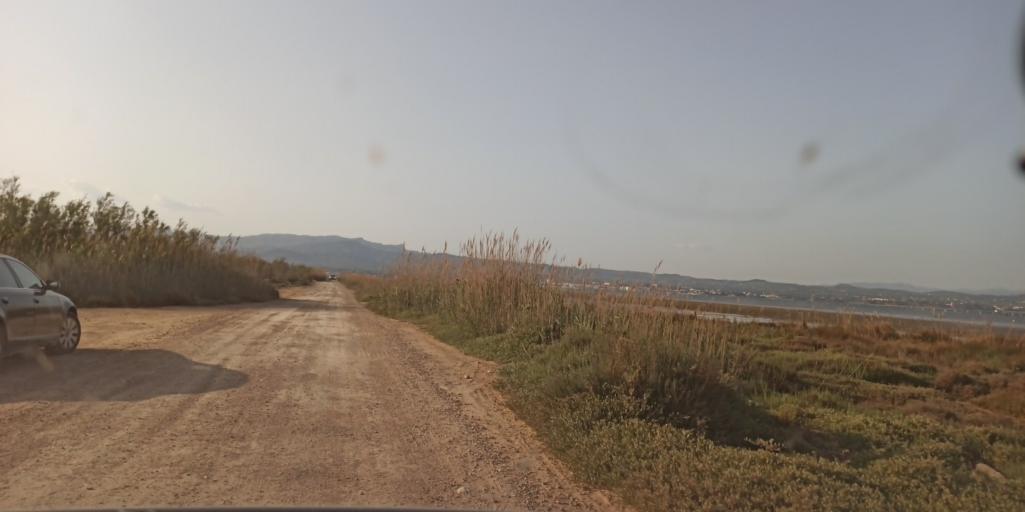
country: ES
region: Catalonia
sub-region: Provincia de Tarragona
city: L'Ampolla
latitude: 40.7753
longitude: 0.7244
